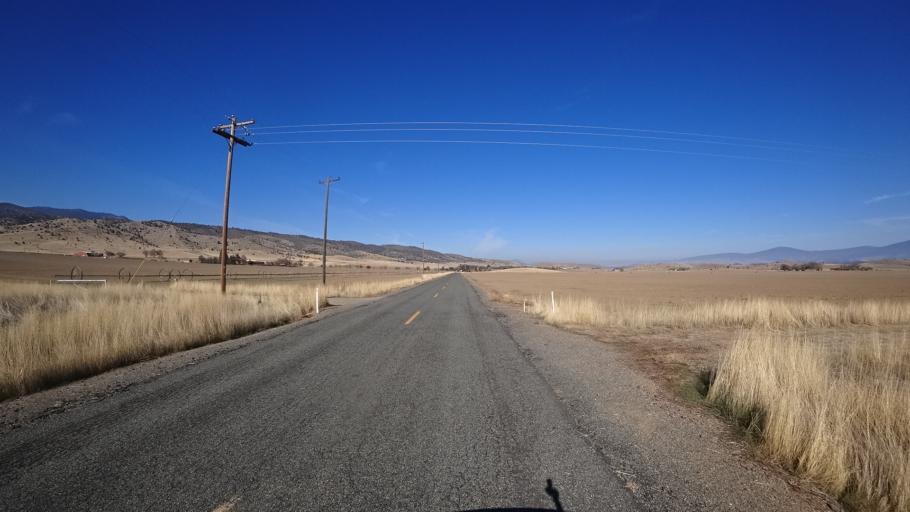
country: US
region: California
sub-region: Siskiyou County
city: Montague
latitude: 41.5679
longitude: -122.5490
